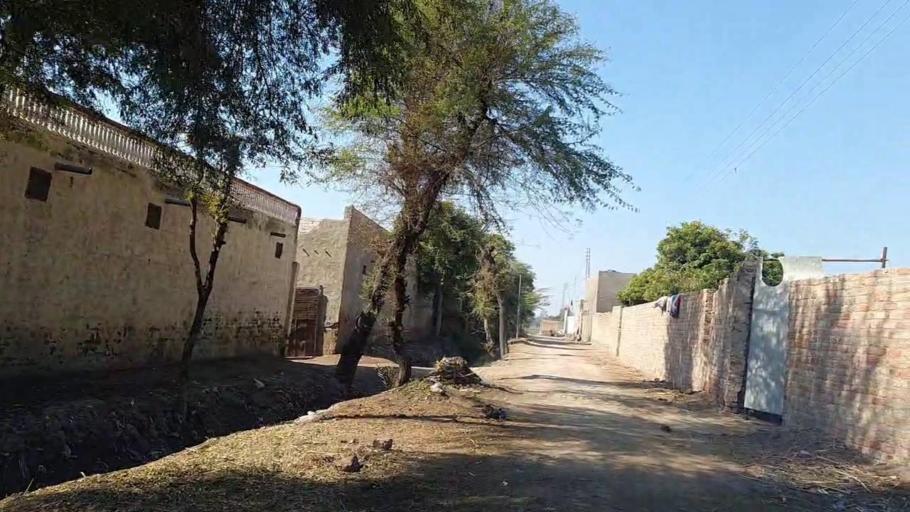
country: PK
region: Sindh
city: Nawabshah
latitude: 26.2893
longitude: 68.3777
